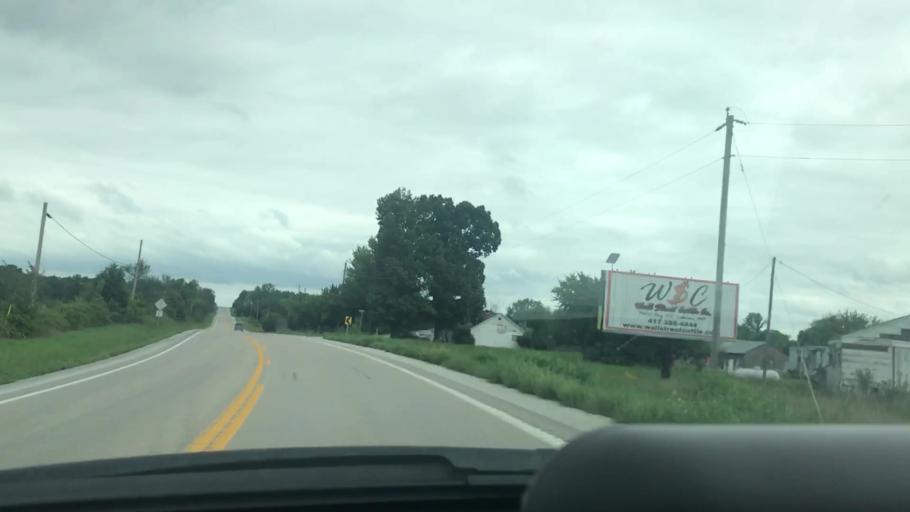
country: US
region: Missouri
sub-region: Dallas County
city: Buffalo
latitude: 37.6954
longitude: -93.1029
